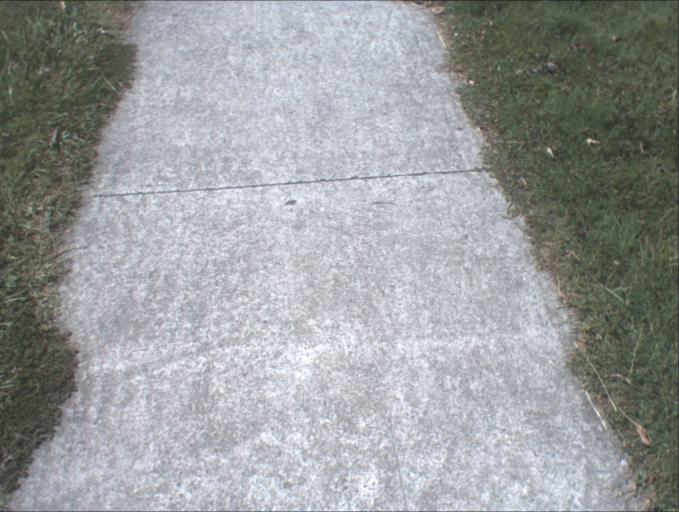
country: AU
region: Queensland
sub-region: Logan
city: Windaroo
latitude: -27.7349
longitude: 153.1937
